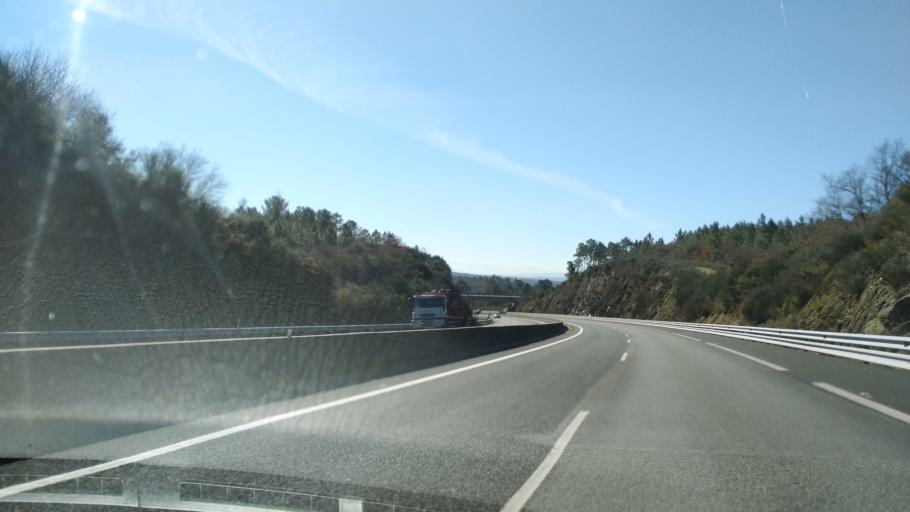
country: ES
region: Galicia
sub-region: Provincia de Ourense
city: Pinor
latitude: 42.5013
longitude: -8.0279
